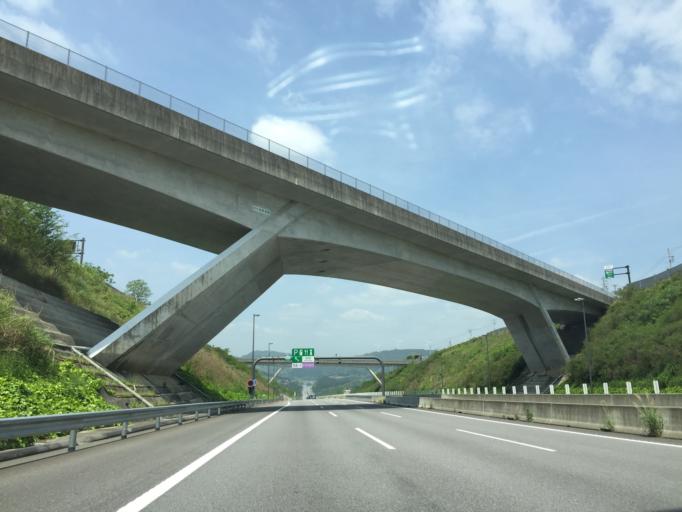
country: JP
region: Shizuoka
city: Hamakita
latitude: 34.8390
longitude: 137.7609
